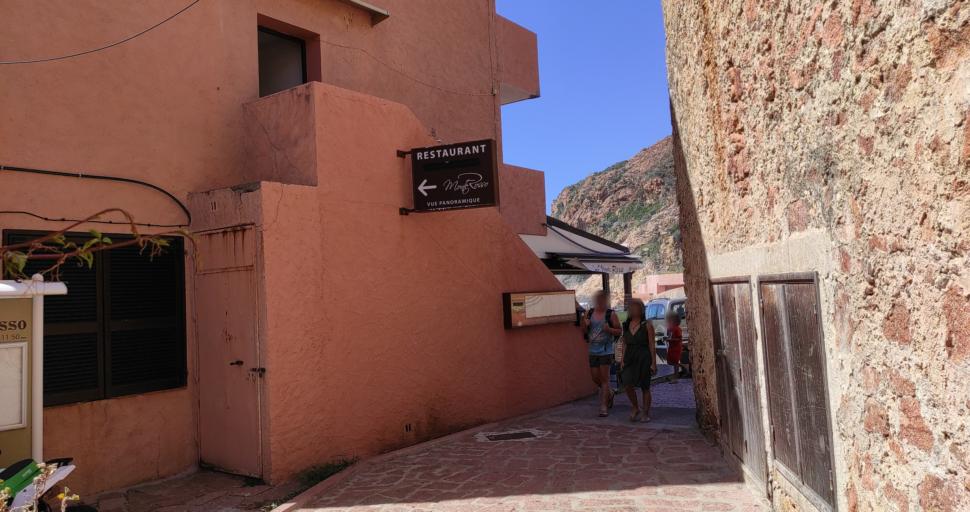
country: FR
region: Corsica
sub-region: Departement de la Corse-du-Sud
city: Cargese
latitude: 42.2677
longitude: 8.6935
